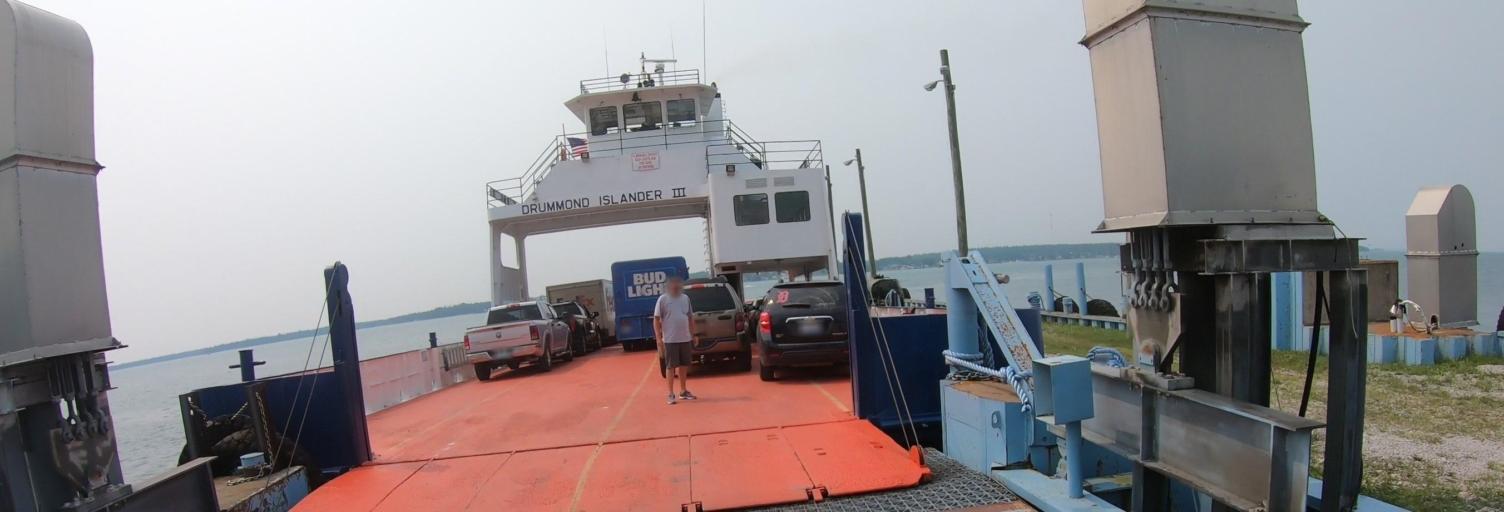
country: CA
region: Ontario
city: Thessalon
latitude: 45.9886
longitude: -83.8785
